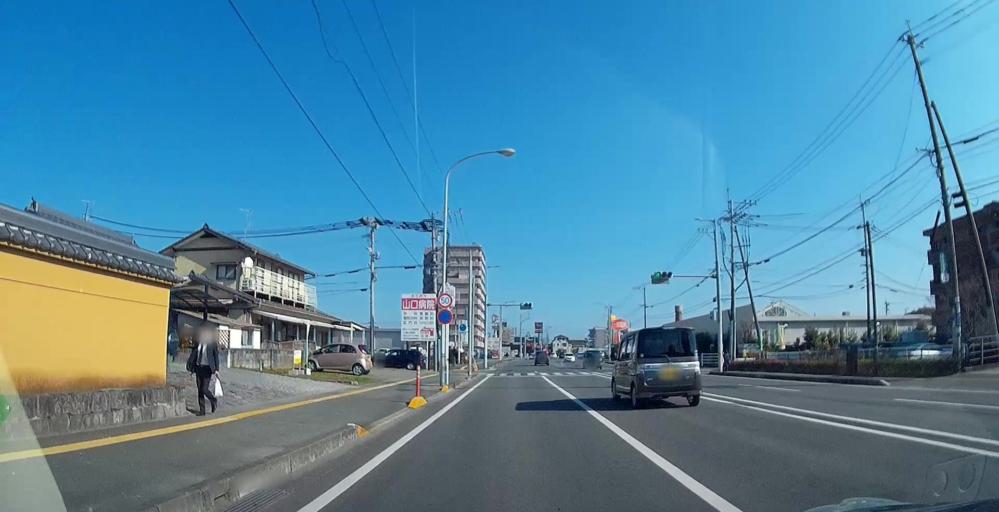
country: JP
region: Kumamoto
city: Kumamoto
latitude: 32.7759
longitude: 130.6784
